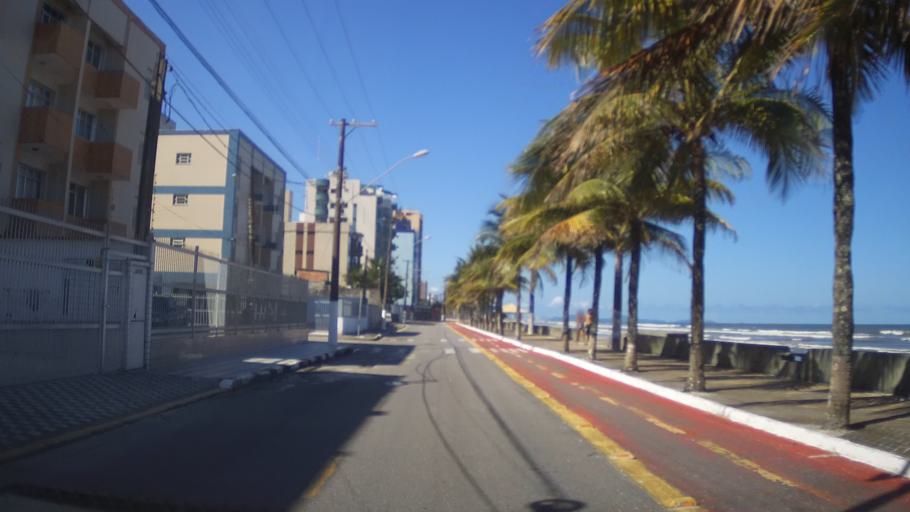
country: BR
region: Sao Paulo
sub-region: Mongagua
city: Mongagua
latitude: -24.0923
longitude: -46.6121
